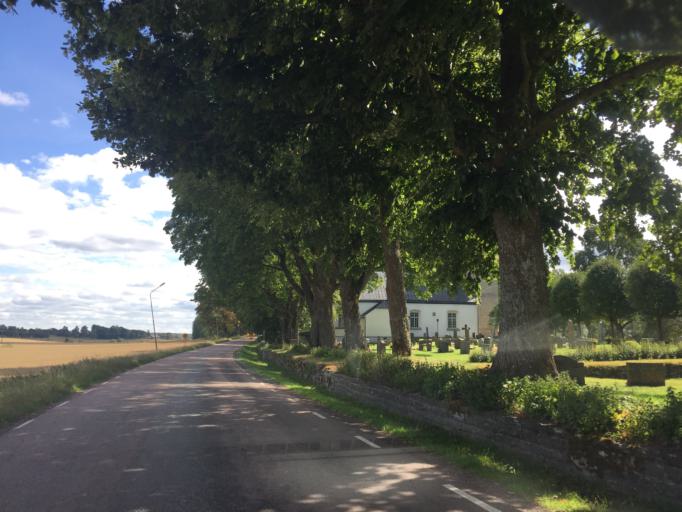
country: SE
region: OErebro
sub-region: Hallsbergs Kommun
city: Hallsberg
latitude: 59.1065
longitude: 15.0053
